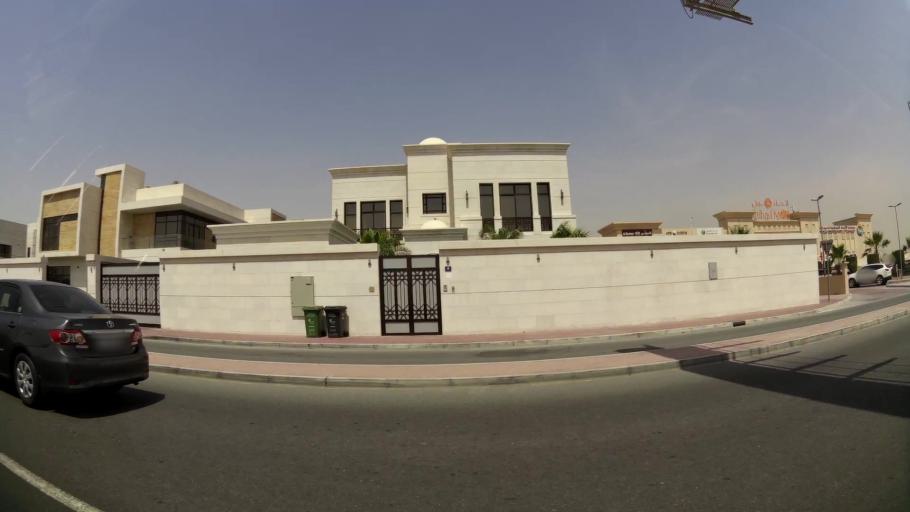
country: AE
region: Ash Shariqah
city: Sharjah
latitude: 25.2378
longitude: 55.4194
